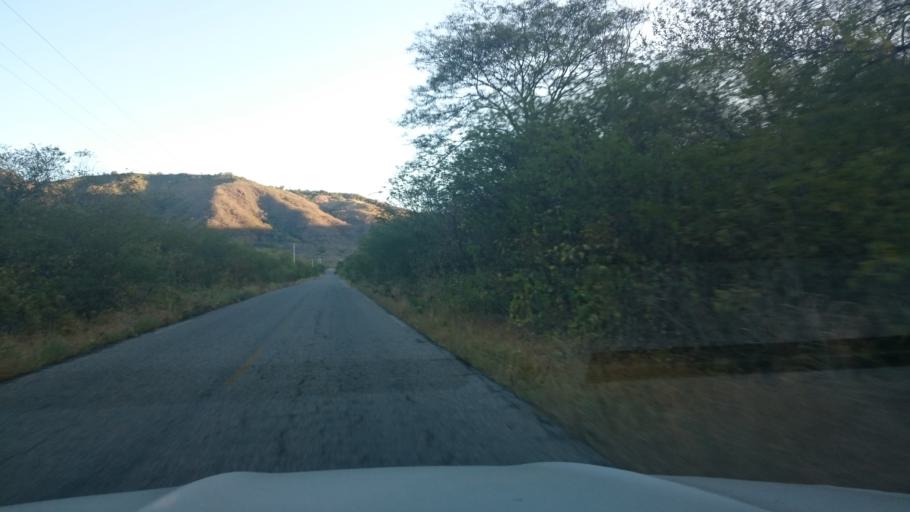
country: BR
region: Rio Grande do Norte
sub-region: Umarizal
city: Umarizal
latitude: -6.0047
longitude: -37.9763
